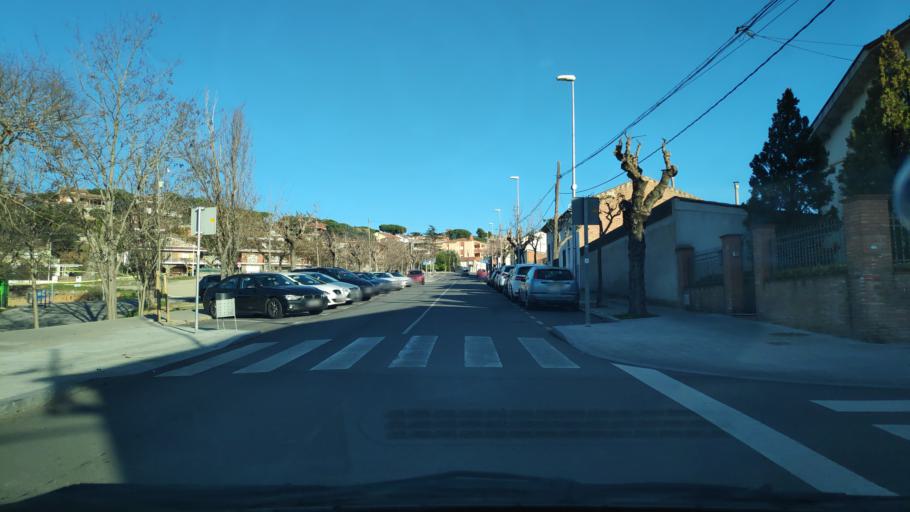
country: ES
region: Catalonia
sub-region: Provincia de Barcelona
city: Mollet del Valles
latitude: 41.5276
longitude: 2.2289
